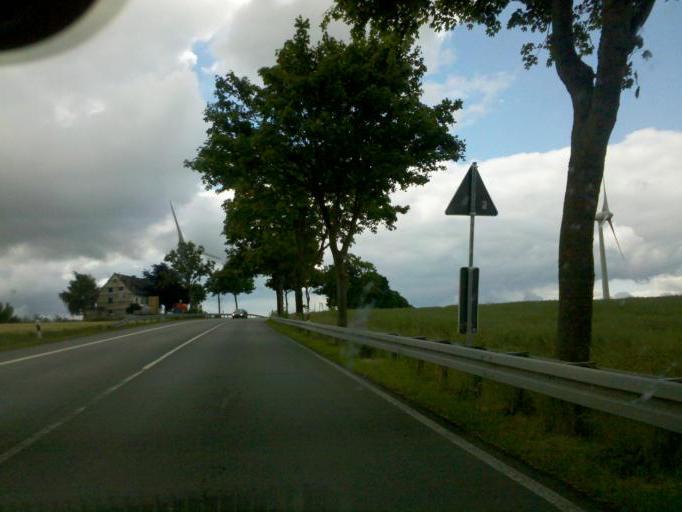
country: DE
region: North Rhine-Westphalia
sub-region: Regierungsbezirk Arnsberg
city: Anrochte
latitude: 51.5115
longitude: 8.3357
